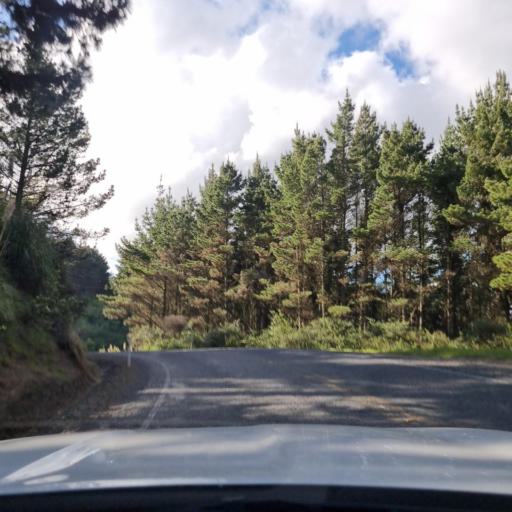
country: NZ
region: Northland
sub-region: Kaipara District
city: Dargaville
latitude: -36.2458
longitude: 174.0443
